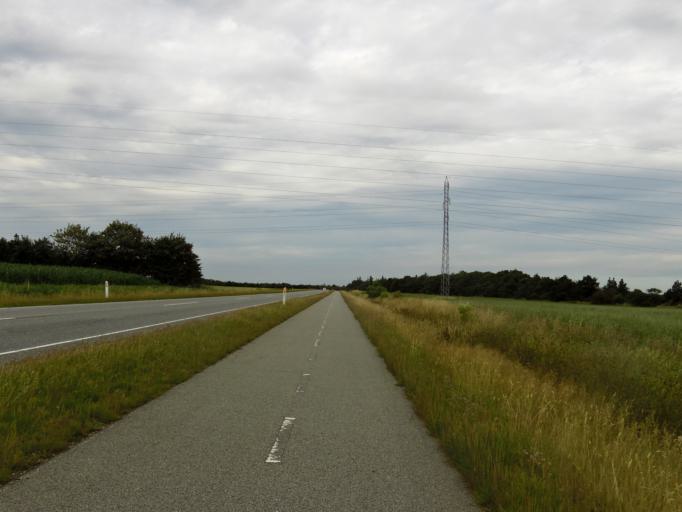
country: DK
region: South Denmark
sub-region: Esbjerg Kommune
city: Ribe
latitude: 55.3124
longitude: 8.8040
